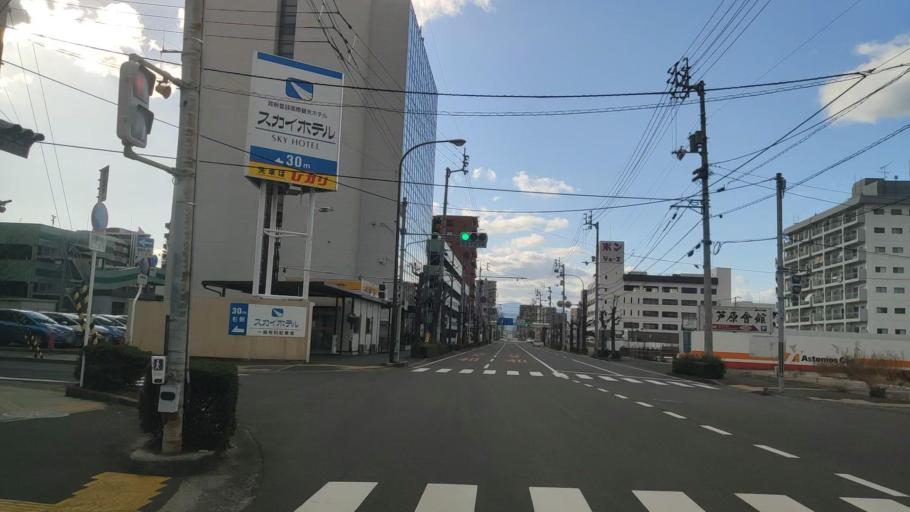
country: JP
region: Ehime
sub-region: Shikoku-chuo Shi
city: Matsuyama
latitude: 33.8390
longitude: 132.7525
